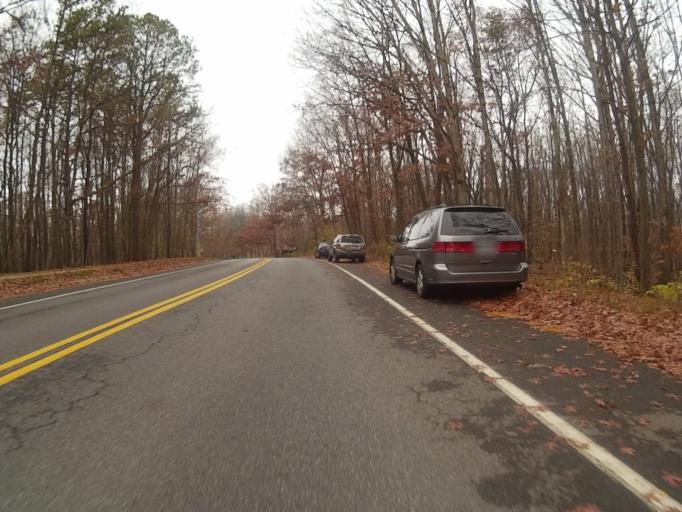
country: US
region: Pennsylvania
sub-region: Centre County
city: Park Forest Village
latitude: 40.8237
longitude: -77.8873
